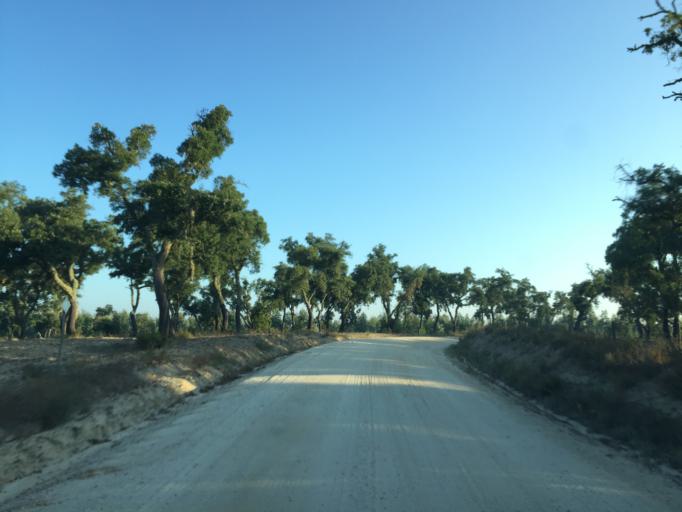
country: PT
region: Portalegre
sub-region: Ponte de Sor
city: Santo Andre
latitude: 39.0867
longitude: -8.3824
